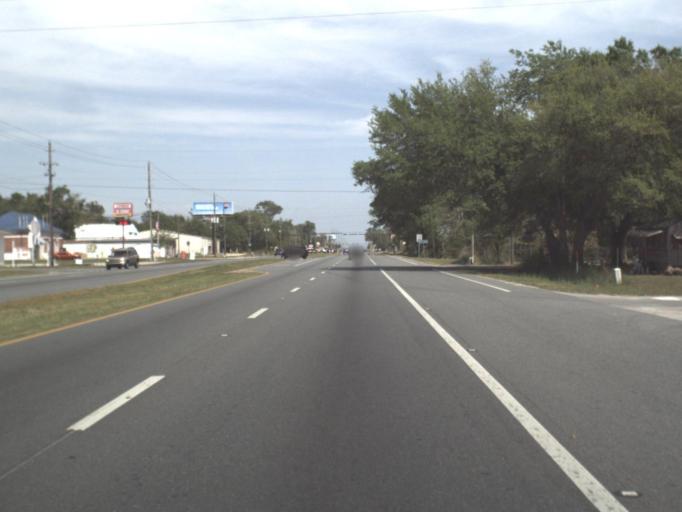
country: US
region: Florida
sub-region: Santa Rosa County
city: Pace
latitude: 30.6035
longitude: -87.1317
